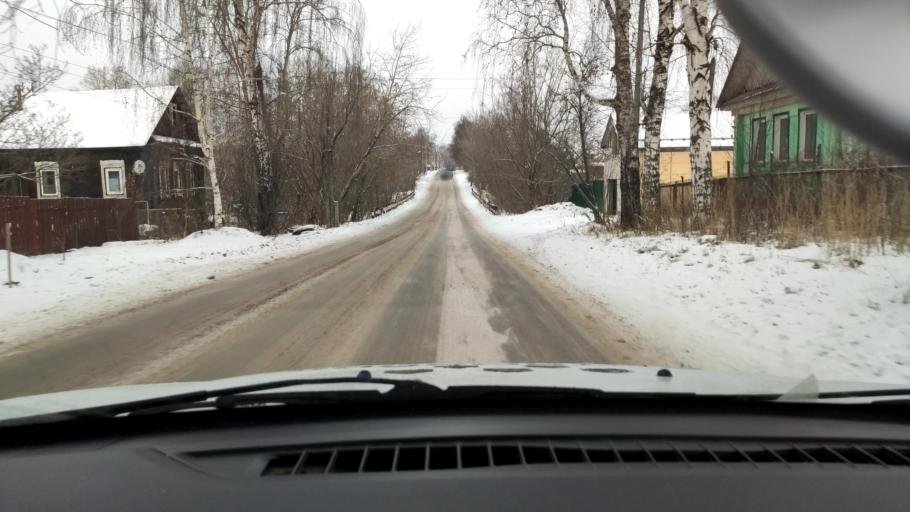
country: RU
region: Perm
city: Polazna
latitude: 58.1200
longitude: 56.3949
